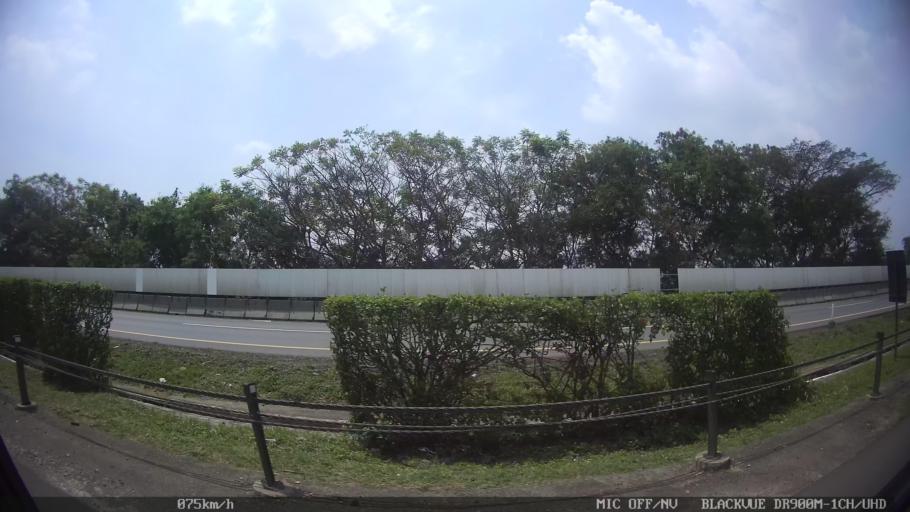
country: ID
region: Banten
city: Serang
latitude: -6.1397
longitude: 106.2633
